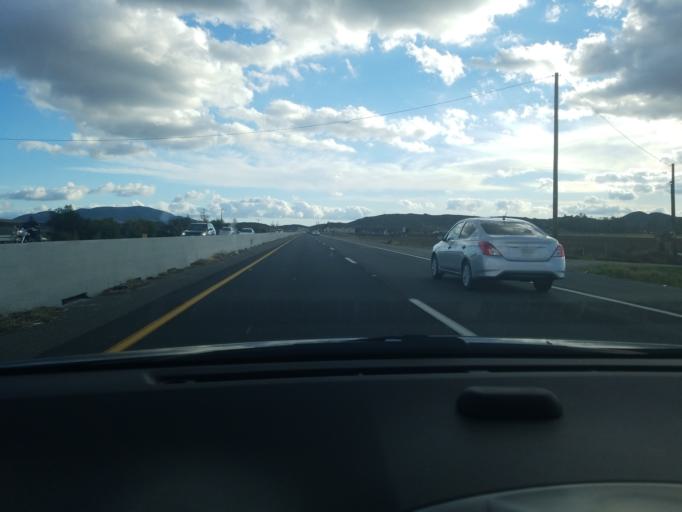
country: US
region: California
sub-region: Riverside County
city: Winchester
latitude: 33.6637
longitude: -117.0848
